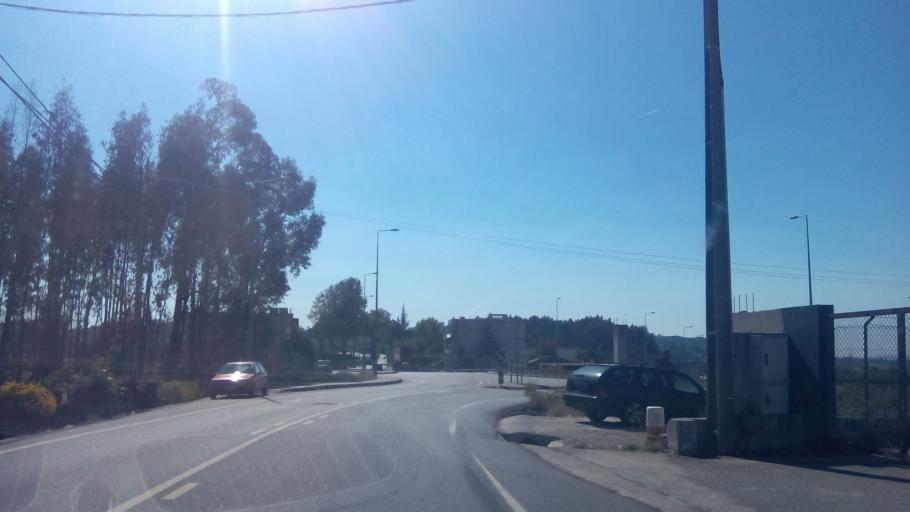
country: PT
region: Porto
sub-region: Lousada
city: Meinedo
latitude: 41.2592
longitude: -8.2105
